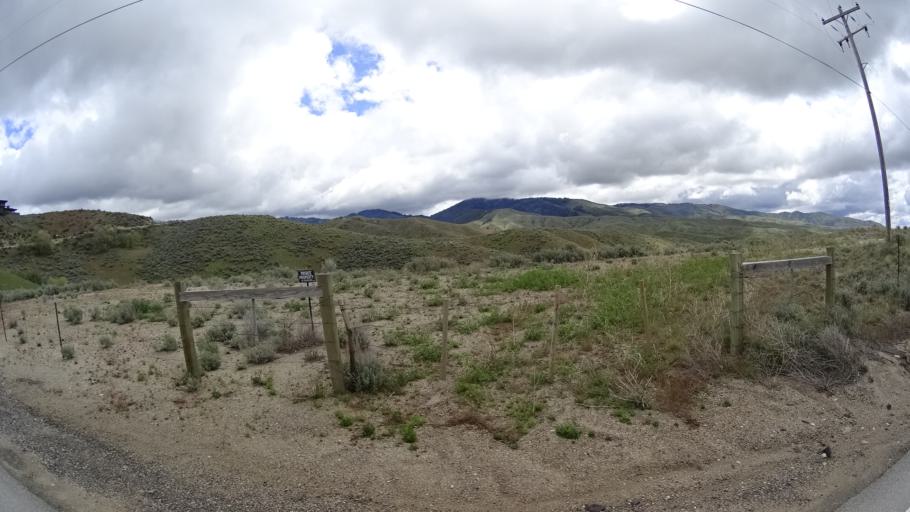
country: US
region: Idaho
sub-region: Ada County
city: Boise
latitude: 43.7099
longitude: -116.1644
